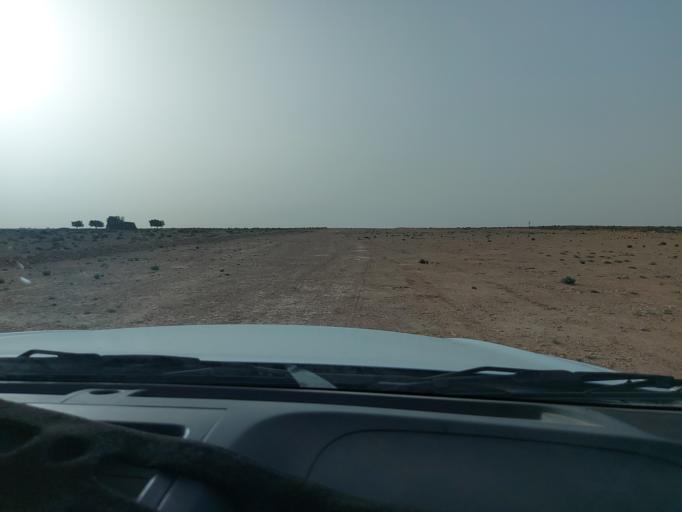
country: TN
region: Madanin
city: Medenine
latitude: 33.3445
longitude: 10.5919
